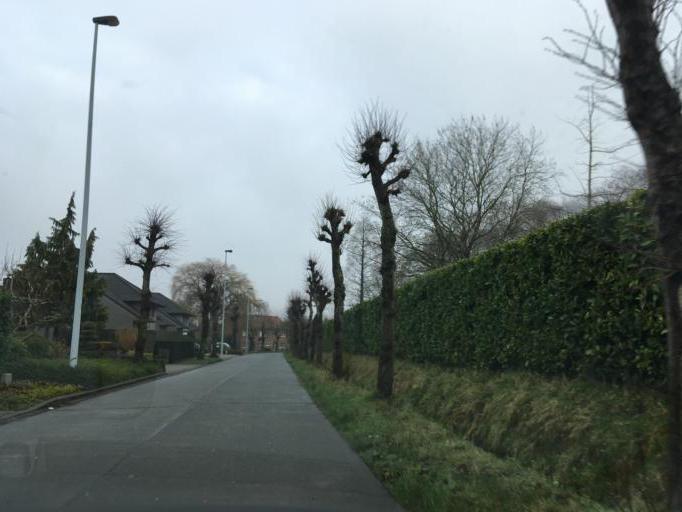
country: BE
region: Flanders
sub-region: Provincie West-Vlaanderen
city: Roeselare
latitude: 50.9319
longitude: 3.1120
